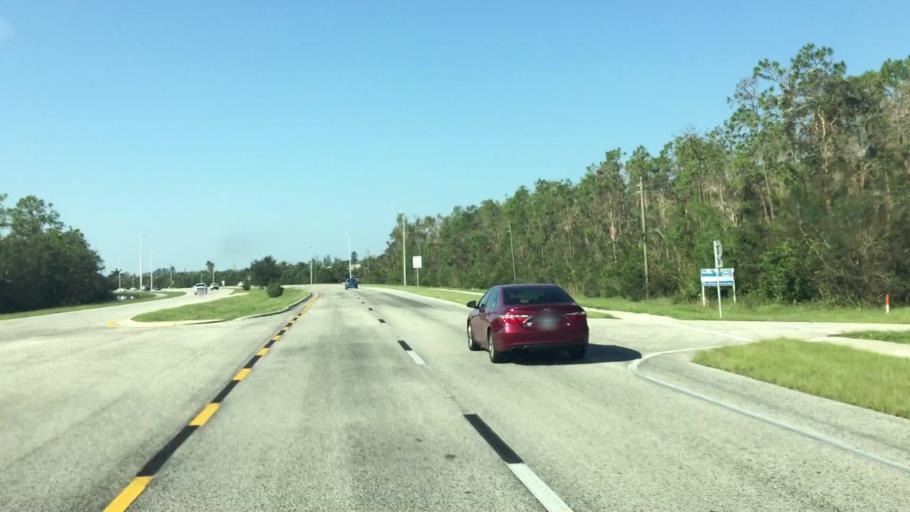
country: US
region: Florida
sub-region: Lee County
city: Villas
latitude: 26.5541
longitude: -81.8365
